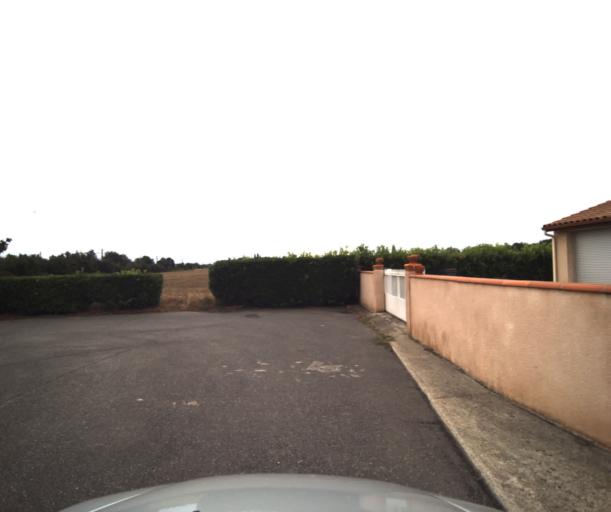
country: FR
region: Midi-Pyrenees
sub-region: Departement de la Haute-Garonne
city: Muret
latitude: 43.4546
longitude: 1.3156
